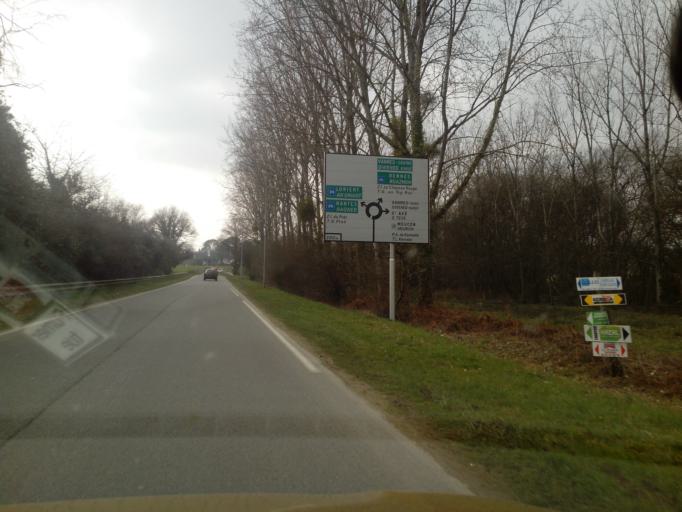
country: FR
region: Brittany
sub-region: Departement du Morbihan
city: Vannes
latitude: 47.6719
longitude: -2.7213
